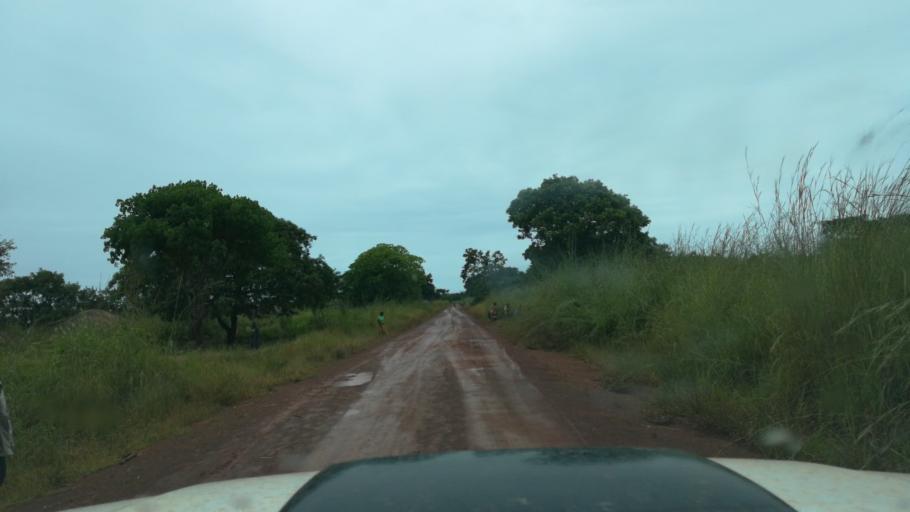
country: ZM
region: Luapula
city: Mwense
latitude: -10.1499
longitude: 28.1231
